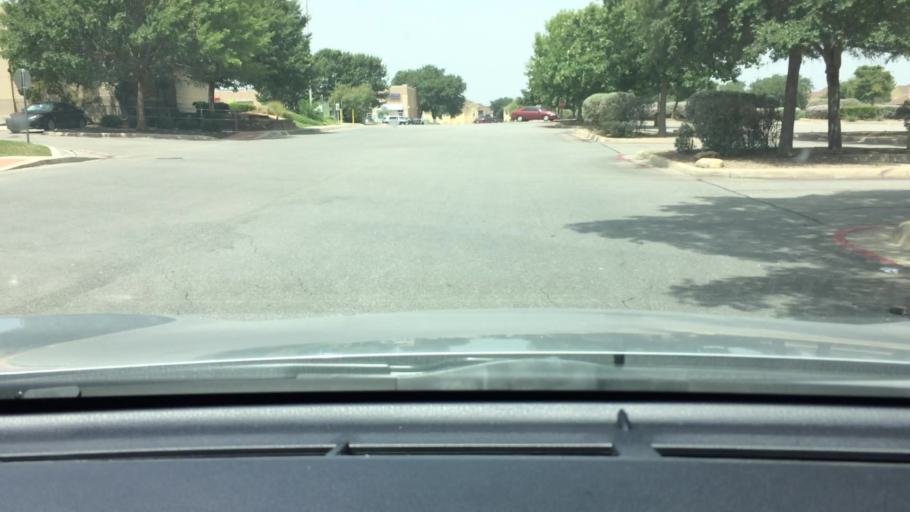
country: US
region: Texas
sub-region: Bexar County
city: San Antonio
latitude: 29.3527
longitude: -98.4409
